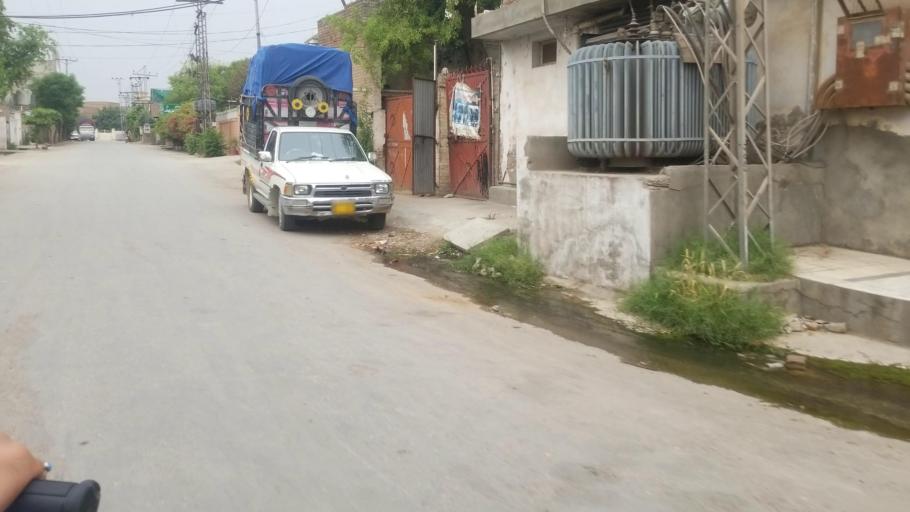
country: PK
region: Khyber Pakhtunkhwa
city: Peshawar
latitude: 33.9835
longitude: 71.5598
